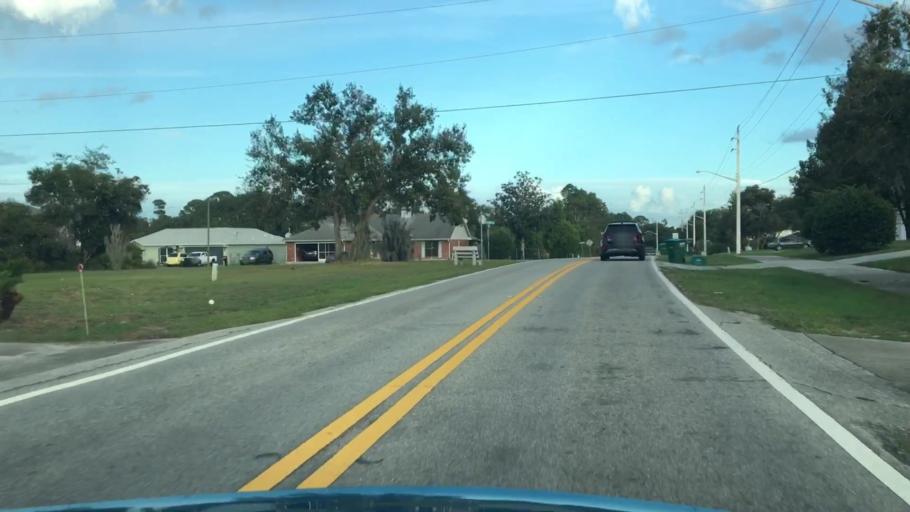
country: US
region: Florida
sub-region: Volusia County
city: Deltona
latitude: 28.9206
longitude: -81.2022
